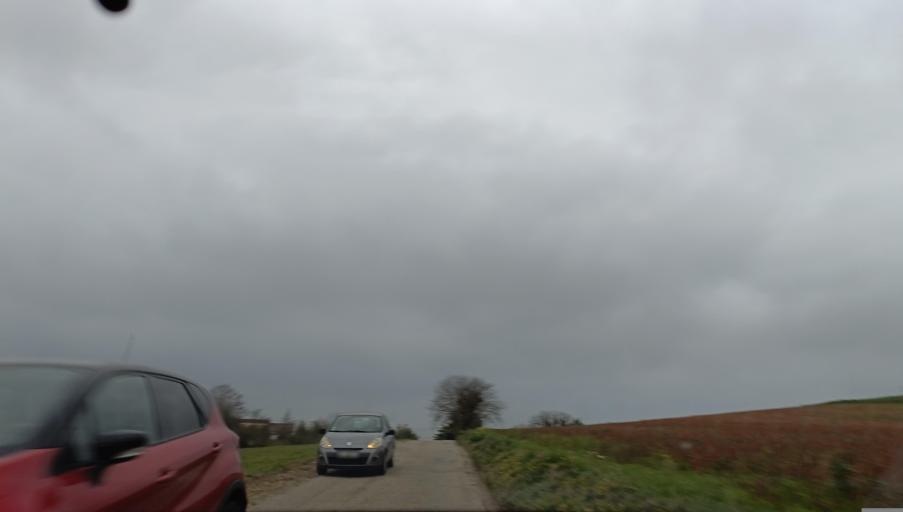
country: FR
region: Rhone-Alpes
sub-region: Departement de l'Isere
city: Chuzelles
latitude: 45.5697
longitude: 4.8721
